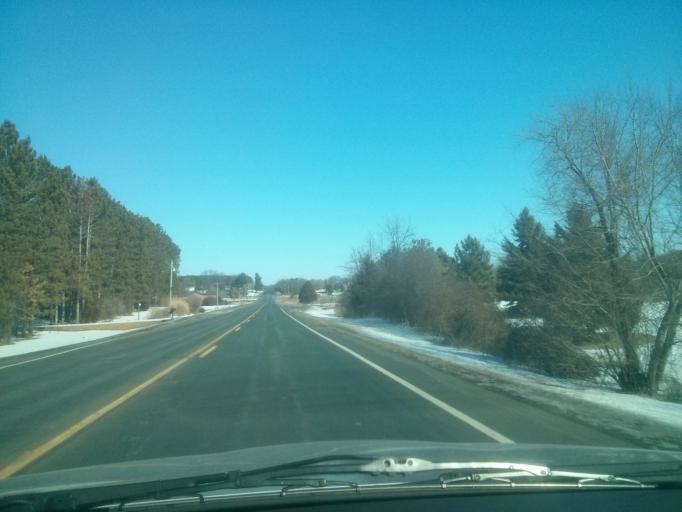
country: US
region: Minnesota
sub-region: Washington County
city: Bayport
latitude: 45.0525
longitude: -92.7409
